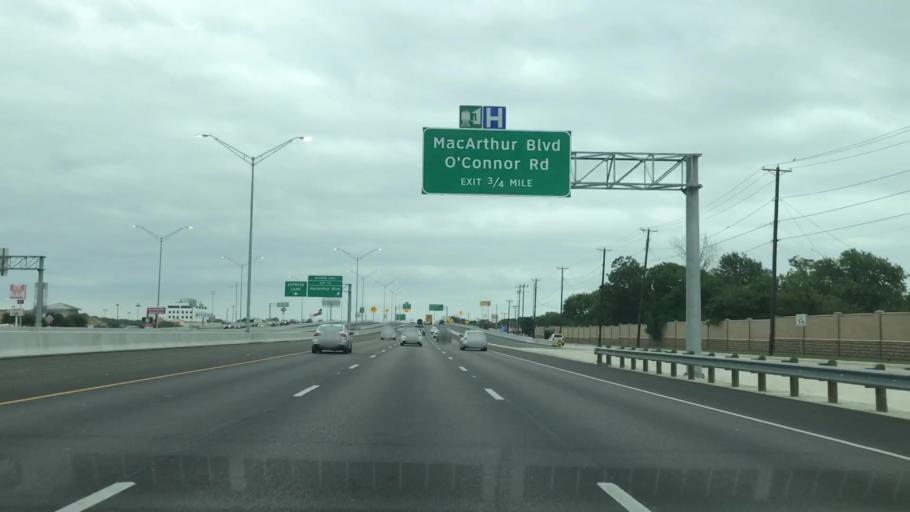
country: US
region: Texas
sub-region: Dallas County
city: Irving
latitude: 32.8369
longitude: -96.9817
